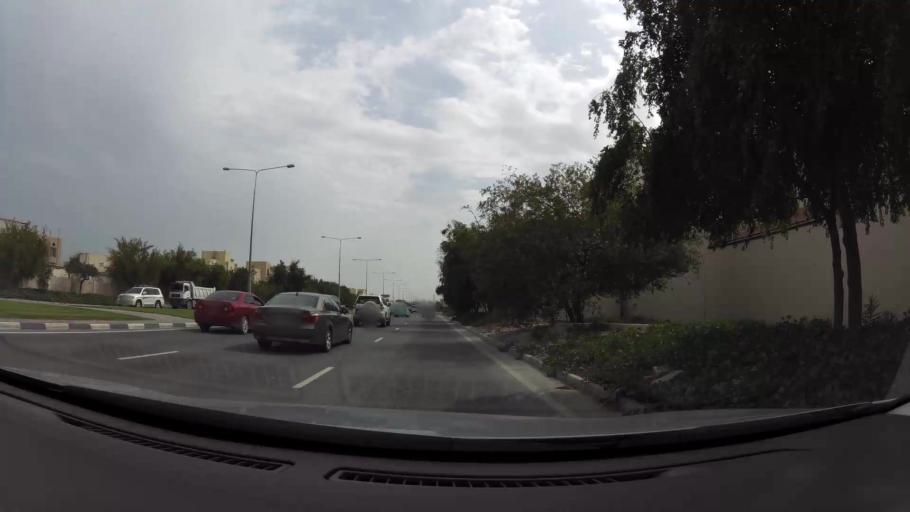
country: QA
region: Baladiyat ad Dawhah
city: Doha
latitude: 25.3399
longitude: 51.5058
